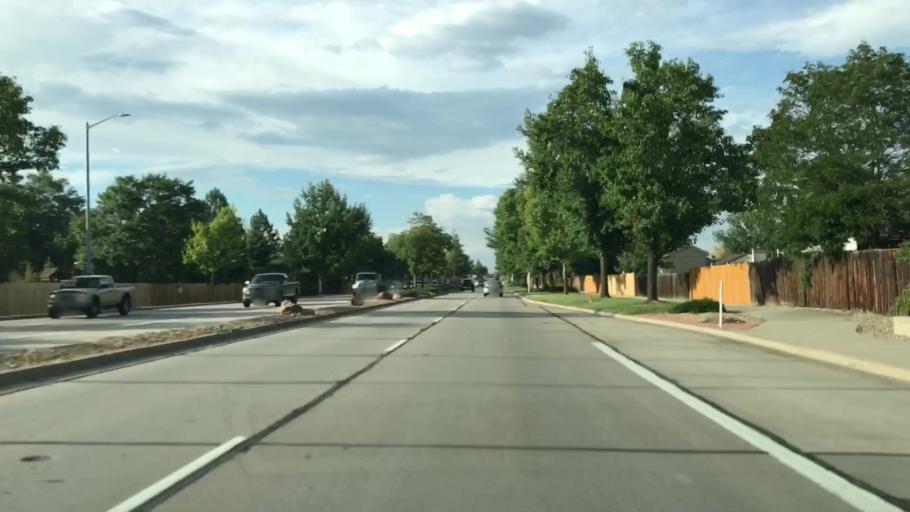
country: US
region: Colorado
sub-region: Boulder County
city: Longmont
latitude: 40.1964
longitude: -105.1308
